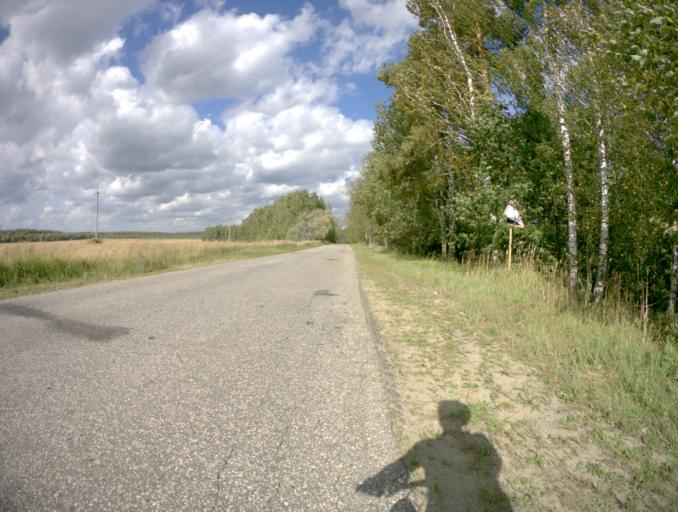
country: RU
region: Vladimir
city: Lakinsk
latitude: 55.9655
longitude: 39.9186
